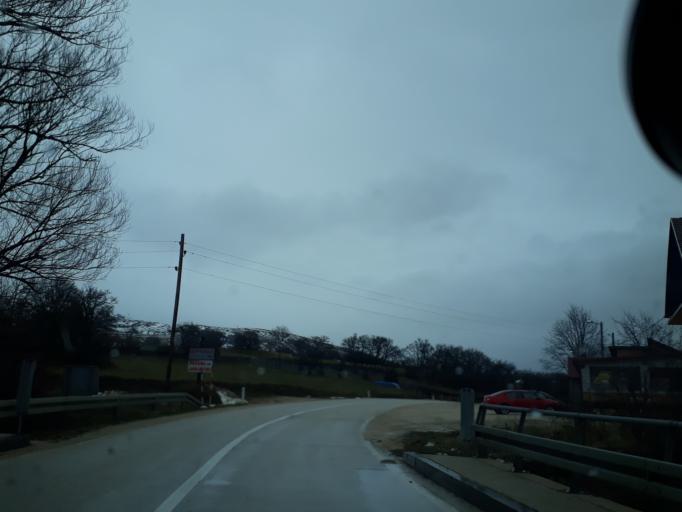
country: BA
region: Federation of Bosnia and Herzegovina
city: Tomislavgrad
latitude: 43.8369
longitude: 17.1862
